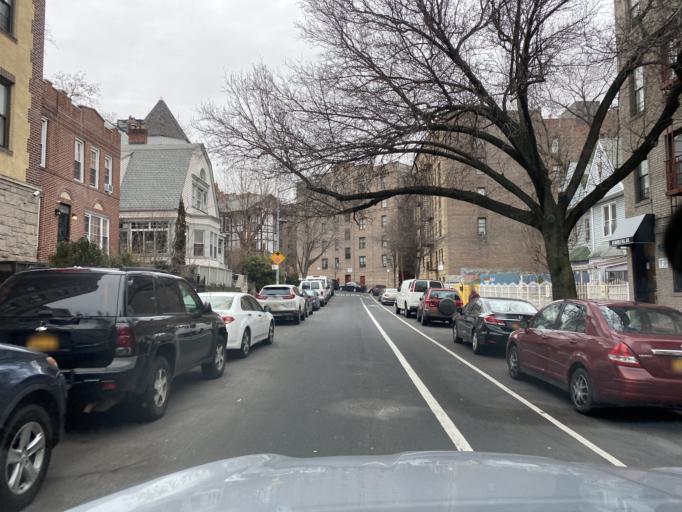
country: US
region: New York
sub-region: New York County
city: Inwood
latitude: 40.8755
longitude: -73.9101
